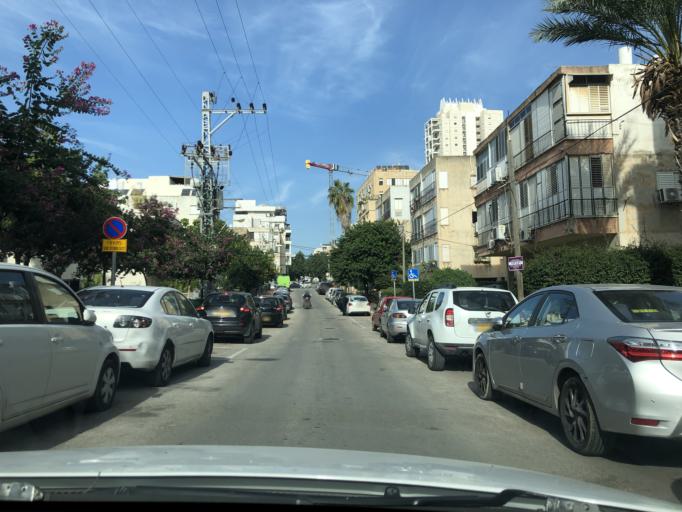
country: IL
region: Tel Aviv
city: Bene Beraq
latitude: 32.0692
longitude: 34.8273
